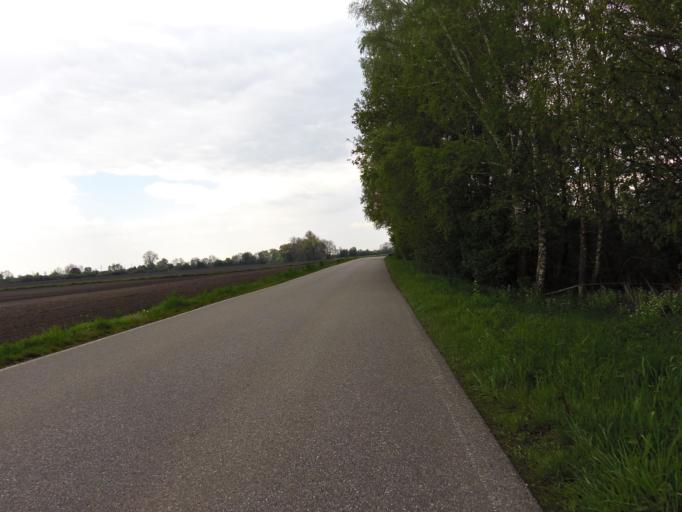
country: DE
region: Bavaria
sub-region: Upper Bavaria
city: Eitting
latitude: 48.3775
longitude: 11.9066
